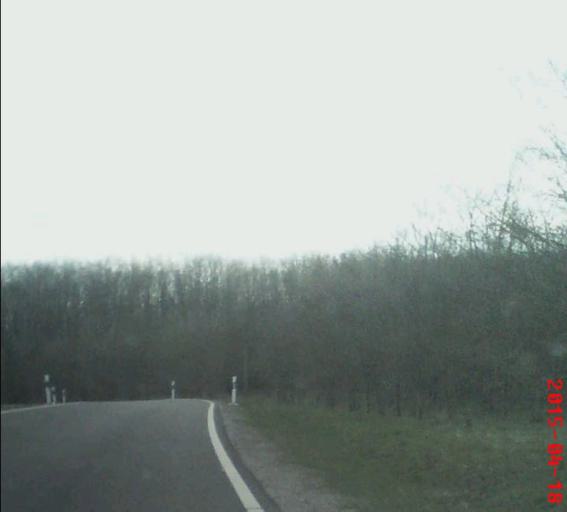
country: DE
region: Thuringia
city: Kreuzebra
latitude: 51.3624
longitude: 10.2648
